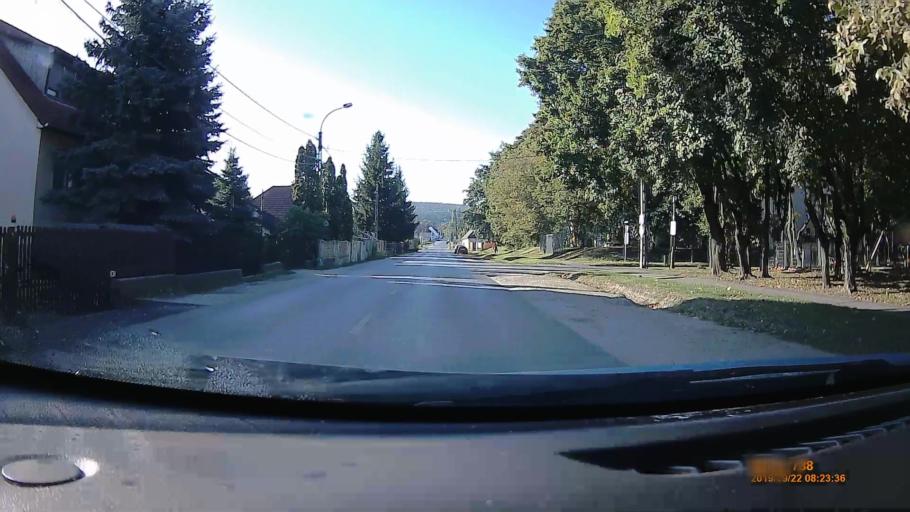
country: HU
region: Borsod-Abauj-Zemplen
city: Miskolc
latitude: 48.0964
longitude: 20.7109
